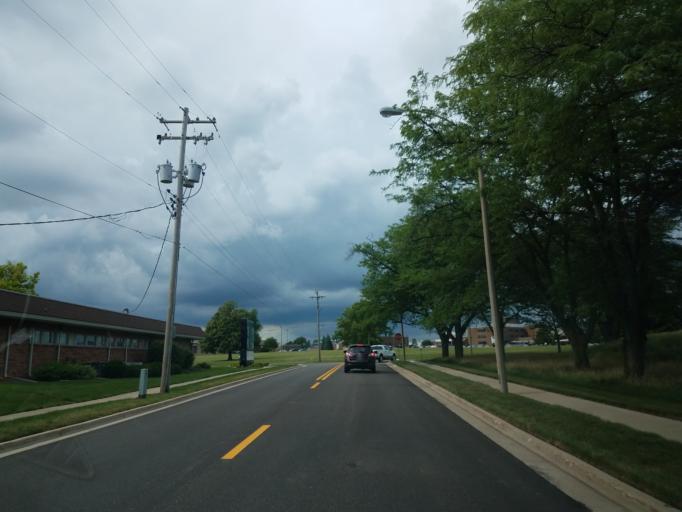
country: US
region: Illinois
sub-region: McLean County
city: Bloomington
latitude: 40.4794
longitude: -88.9571
